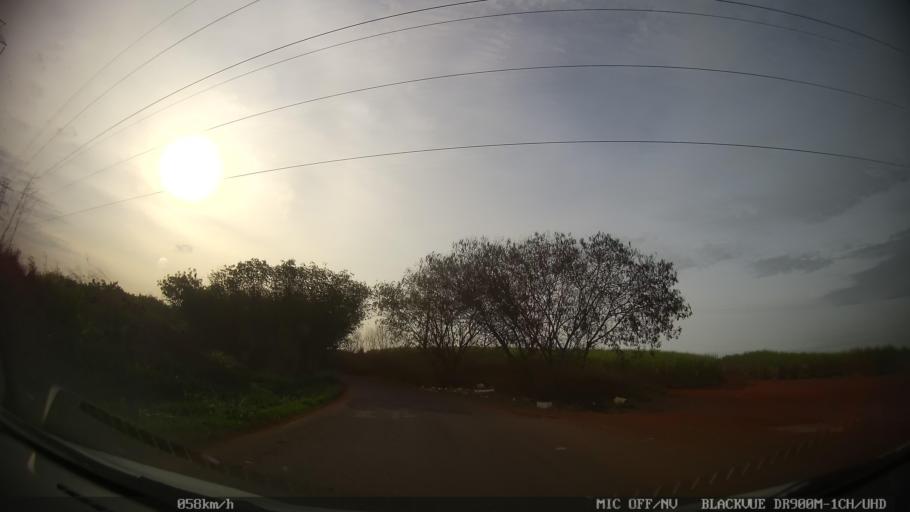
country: BR
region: Sao Paulo
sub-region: Piracicaba
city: Piracicaba
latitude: -22.7098
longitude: -47.5800
